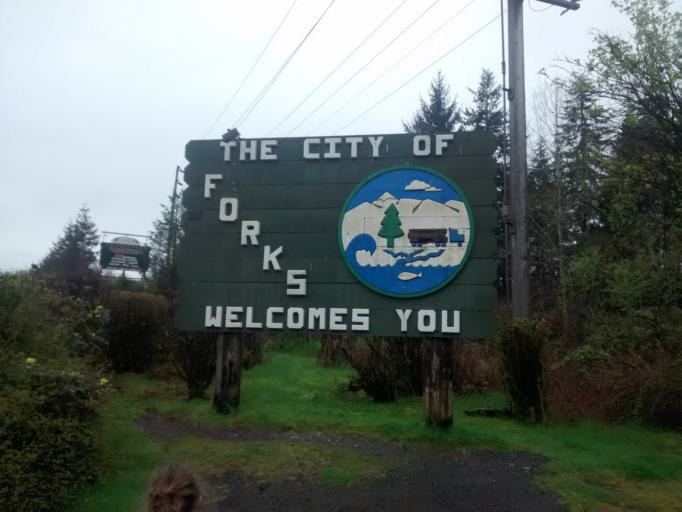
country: US
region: Washington
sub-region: Clallam County
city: Forks
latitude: 47.9590
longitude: -124.3918
